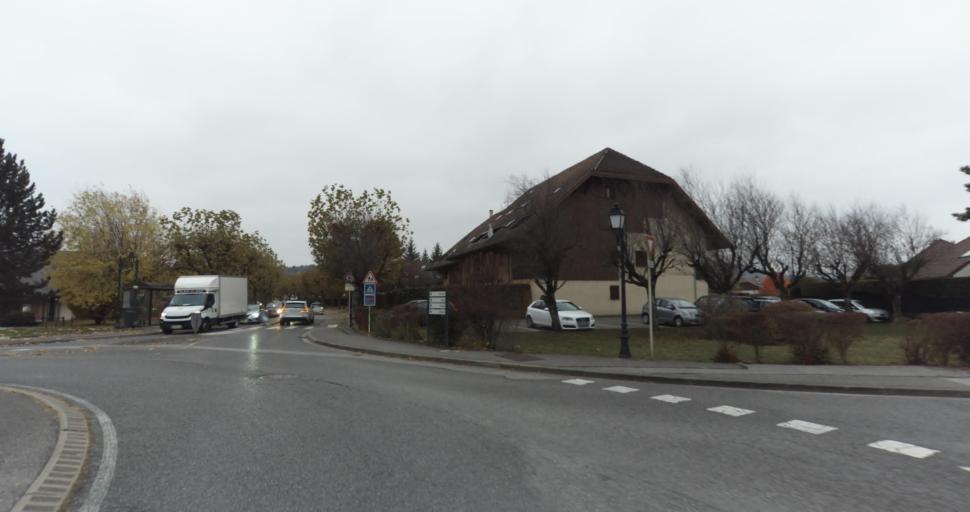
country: FR
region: Rhone-Alpes
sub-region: Departement de la Haute-Savoie
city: Epagny
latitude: 45.9381
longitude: 6.0877
